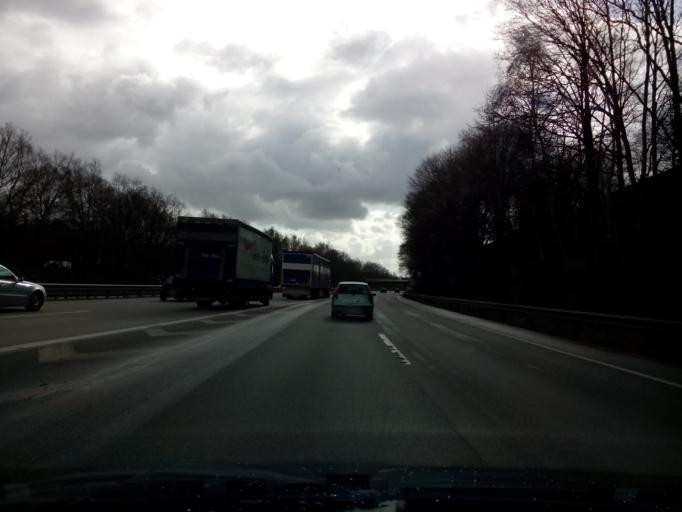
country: DE
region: Lower Saxony
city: Ritterhude
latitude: 53.1758
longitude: 8.7142
